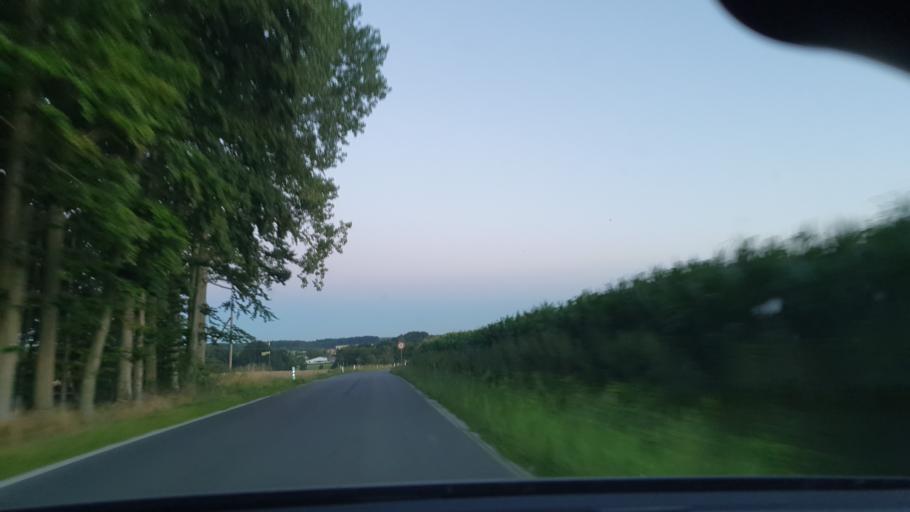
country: DE
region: North Rhine-Westphalia
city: Spenge
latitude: 52.1588
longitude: 8.4610
